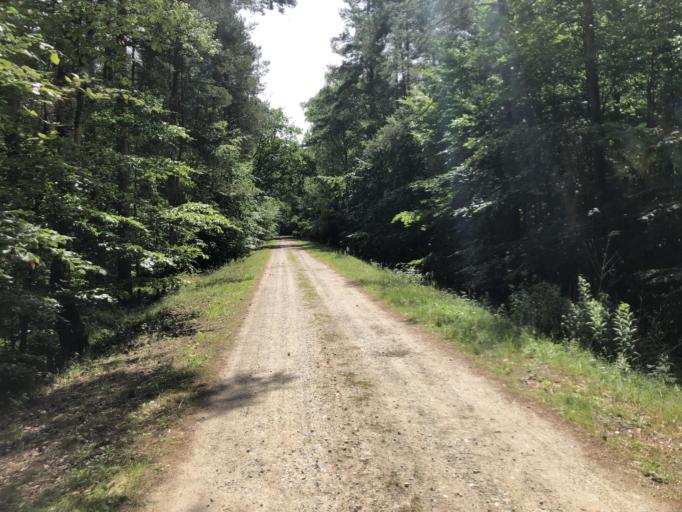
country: DE
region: Lower Saxony
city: Bleckede
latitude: 53.2750
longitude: 10.7647
